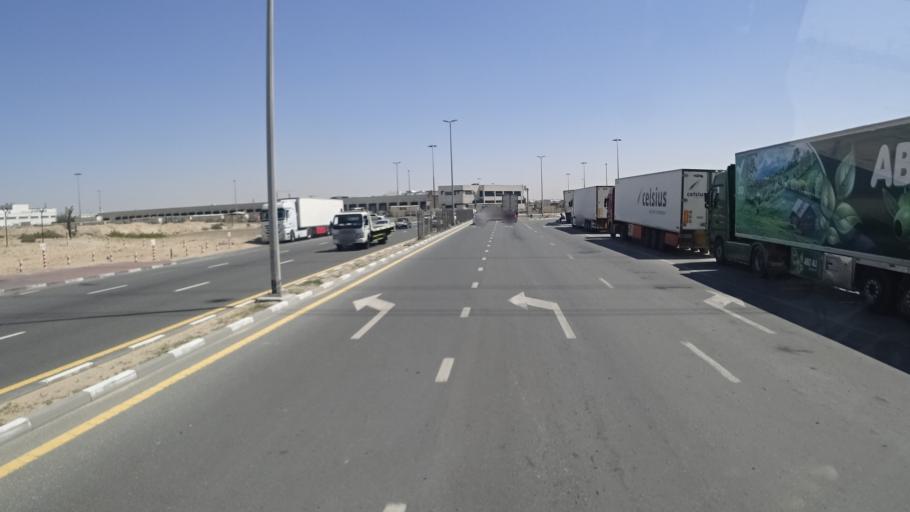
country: AE
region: Ash Shariqah
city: Sharjah
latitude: 25.1733
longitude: 55.3832
